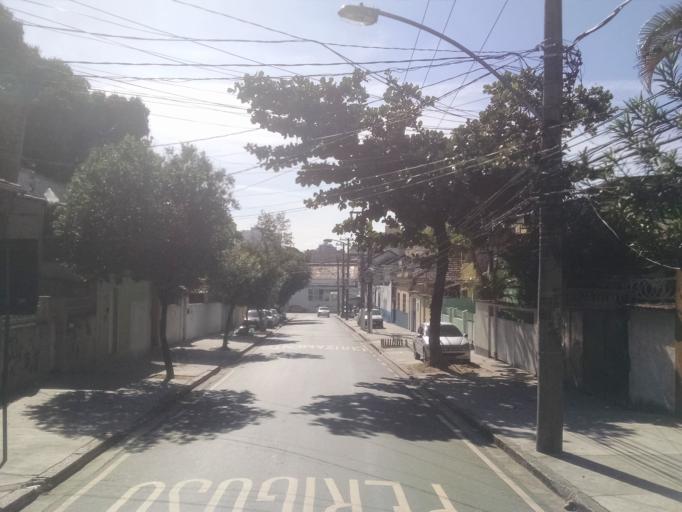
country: BR
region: Rio de Janeiro
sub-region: Rio De Janeiro
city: Rio de Janeiro
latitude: -22.9121
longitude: -43.2701
